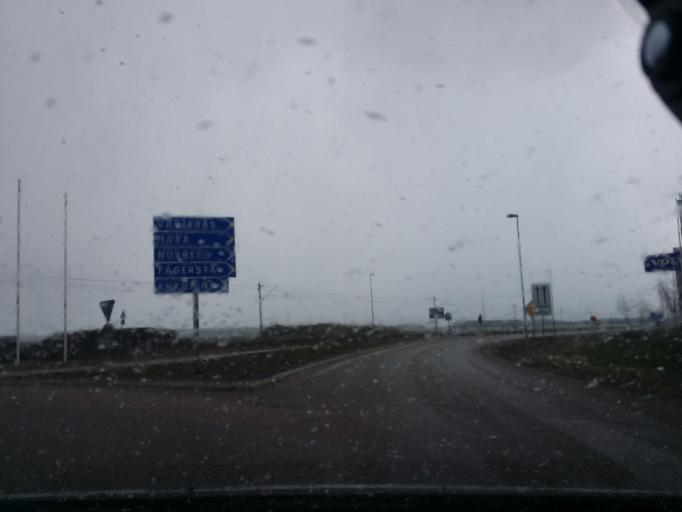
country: SE
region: Vaestmanland
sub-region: Sala Kommun
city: Sala
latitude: 59.9103
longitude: 16.6190
